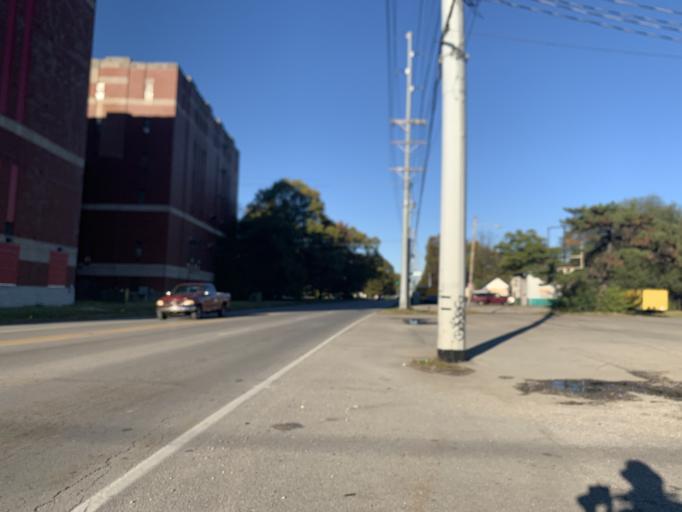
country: US
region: Kentucky
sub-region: Jefferson County
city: Shively
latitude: 38.2136
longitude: -85.7839
